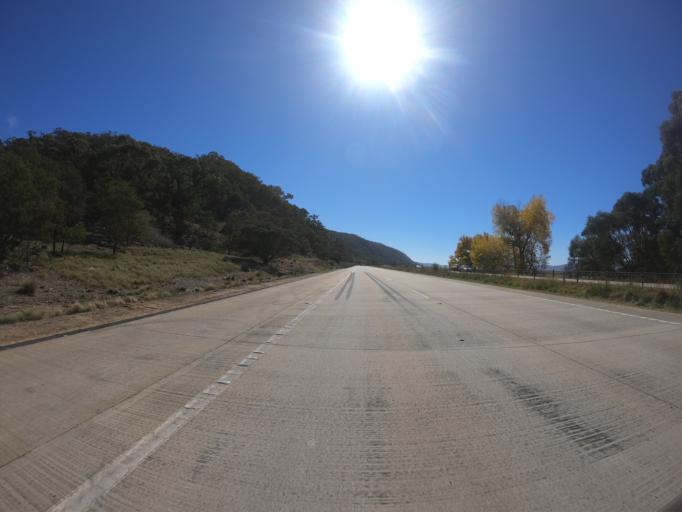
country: AU
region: New South Wales
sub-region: Yass Valley
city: Gundaroo
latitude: -35.0729
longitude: 149.3741
